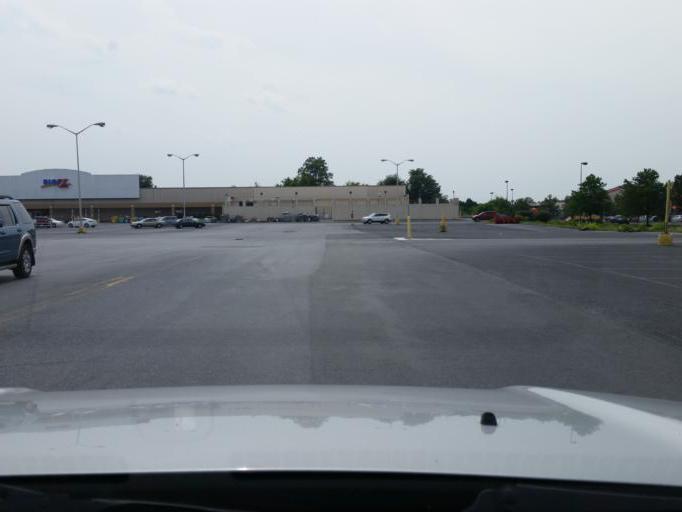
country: US
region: Pennsylvania
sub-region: Cumberland County
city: Mechanicsburg
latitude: 40.2410
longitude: -76.9876
